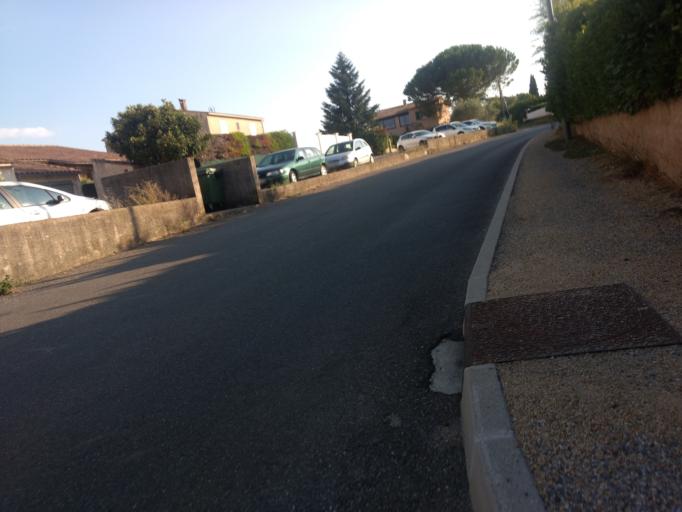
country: FR
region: Provence-Alpes-Cote d'Azur
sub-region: Departement des Alpes-de-Haute-Provence
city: Manosque
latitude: 43.8235
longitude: 5.7755
